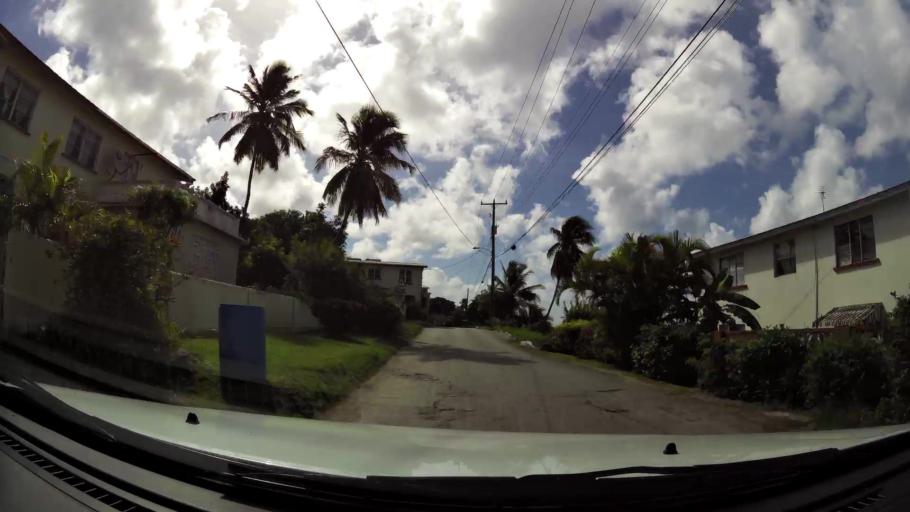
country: BB
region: Saint Lucy
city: Checker Hall
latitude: 13.2758
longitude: -59.6469
